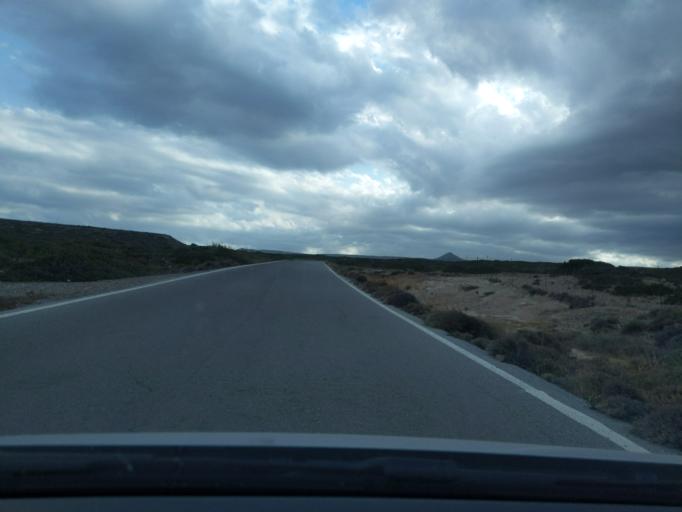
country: GR
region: Crete
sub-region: Nomos Lasithiou
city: Palekastro
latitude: 35.2469
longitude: 26.2500
